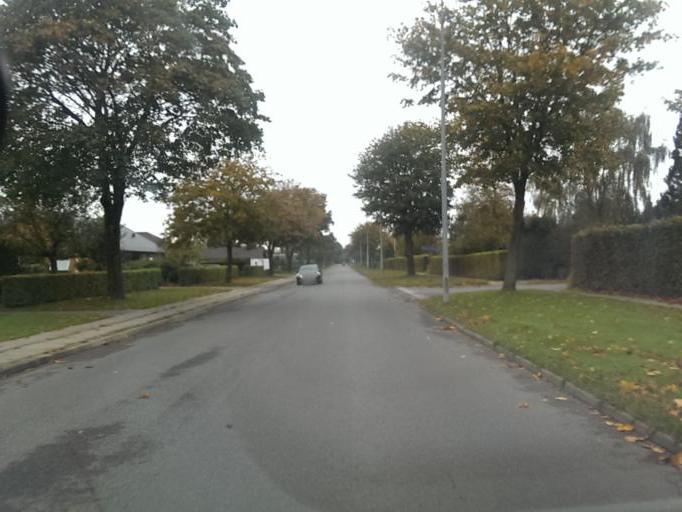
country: DK
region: South Denmark
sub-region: Esbjerg Kommune
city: Bramming
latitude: 55.4660
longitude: 8.7155
